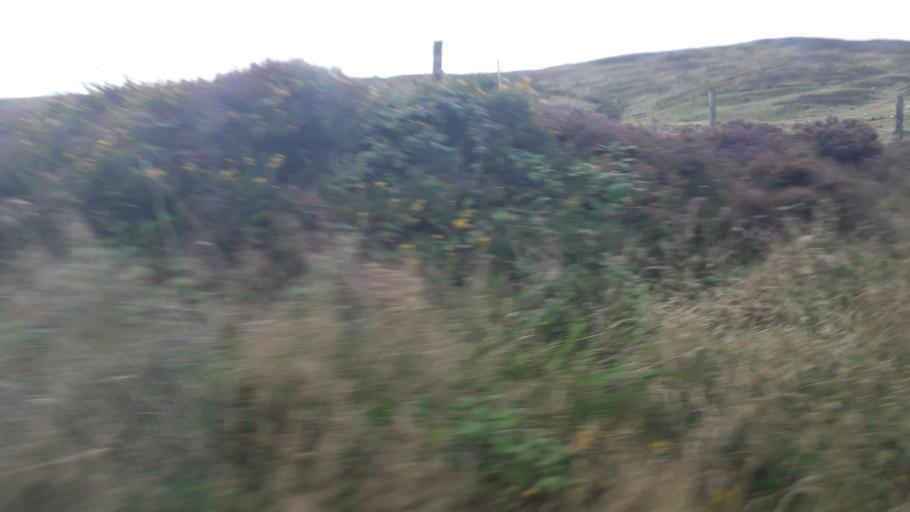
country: GB
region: Northern Ireland
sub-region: Down District
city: Warrenpoint
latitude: 54.0503
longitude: -6.2706
